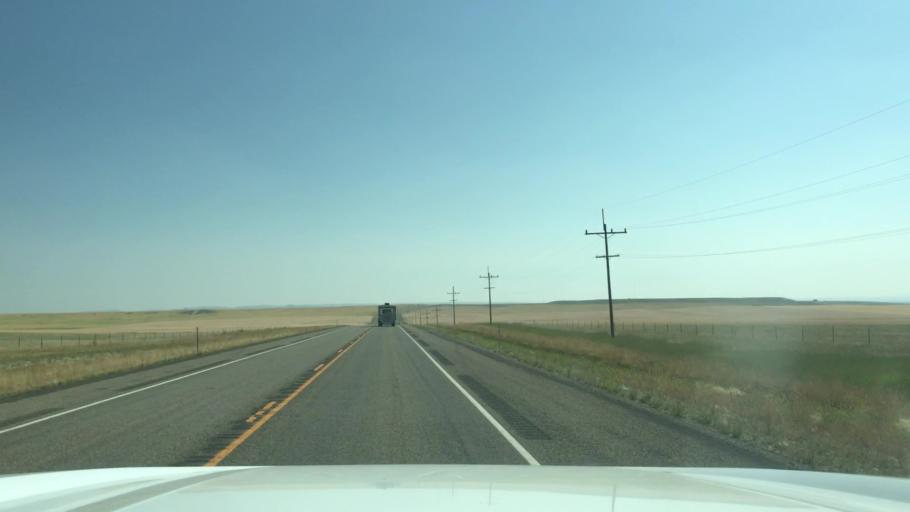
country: US
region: Montana
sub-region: Wheatland County
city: Harlowton
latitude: 46.4948
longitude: -109.7661
